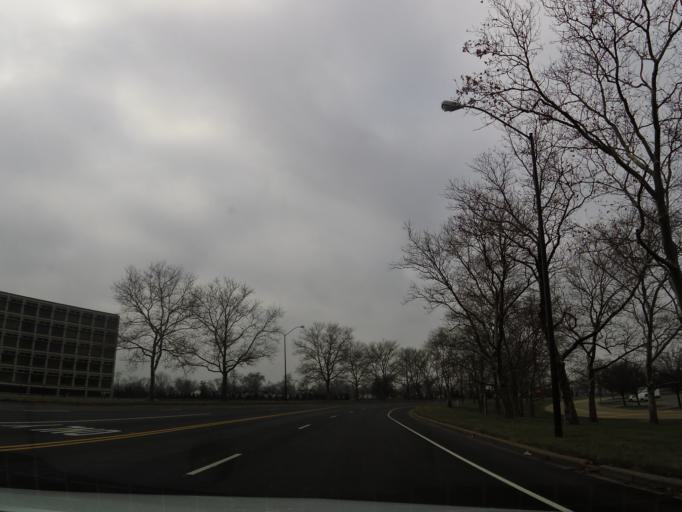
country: US
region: Indiana
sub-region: Bartholomew County
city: Columbus
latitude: 39.2031
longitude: -85.9051
